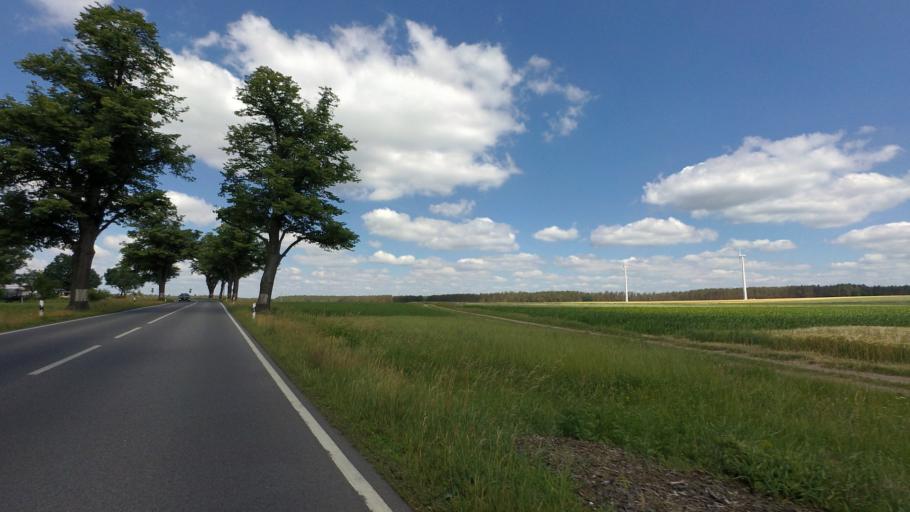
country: DE
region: Brandenburg
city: Finsterwalde
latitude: 51.6309
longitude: 13.7683
